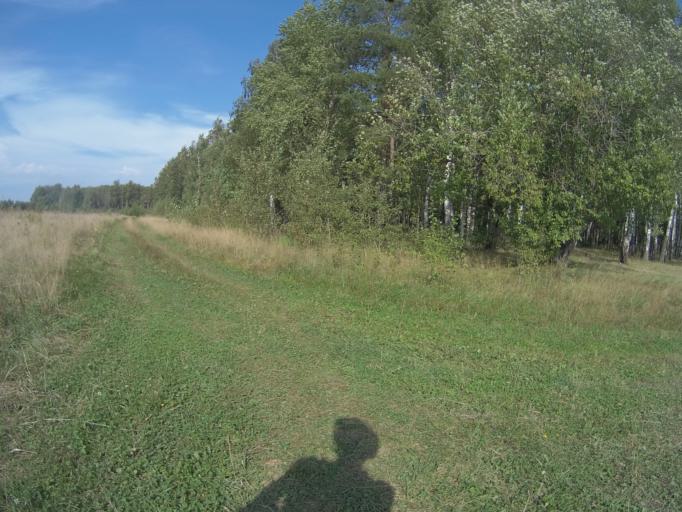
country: RU
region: Vladimir
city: Bogolyubovo
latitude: 56.1168
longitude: 40.5389
